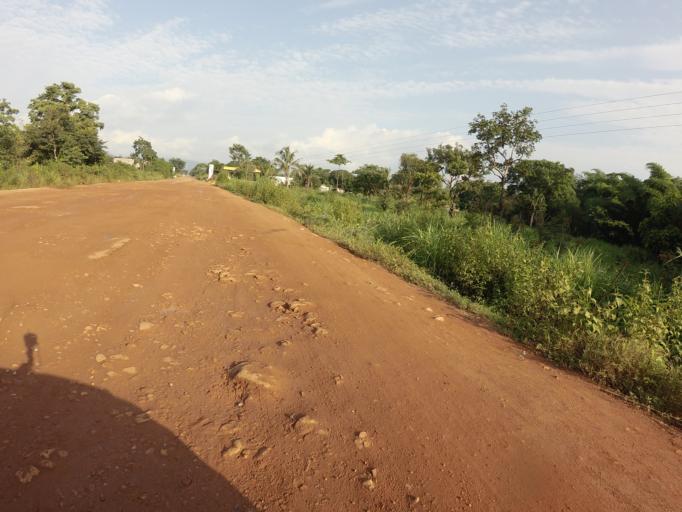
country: GH
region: Volta
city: Kpandu
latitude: 7.0067
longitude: 0.4304
